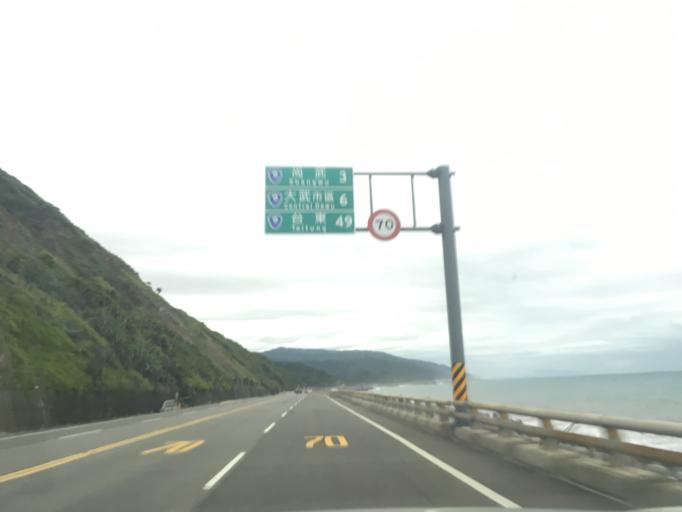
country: TW
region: Taiwan
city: Hengchun
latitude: 22.3145
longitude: 120.8914
